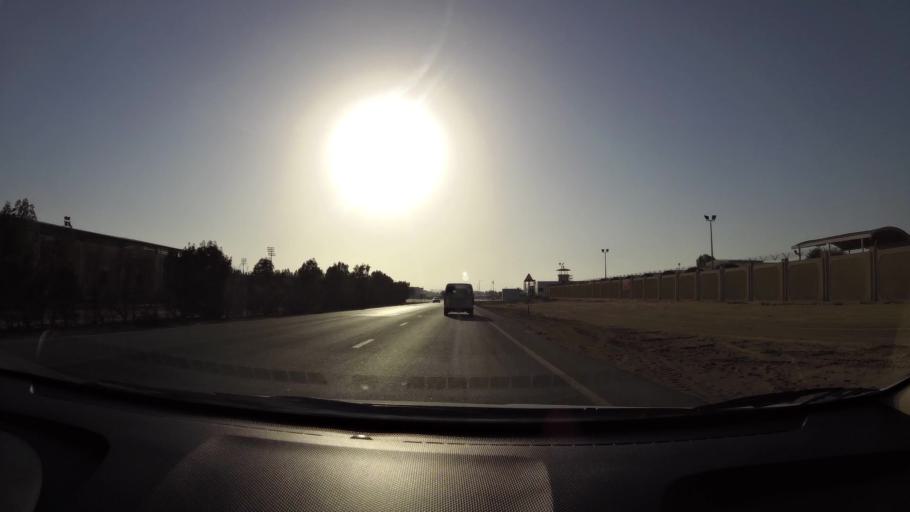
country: AE
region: Ajman
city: Ajman
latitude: 25.4029
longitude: 55.4894
